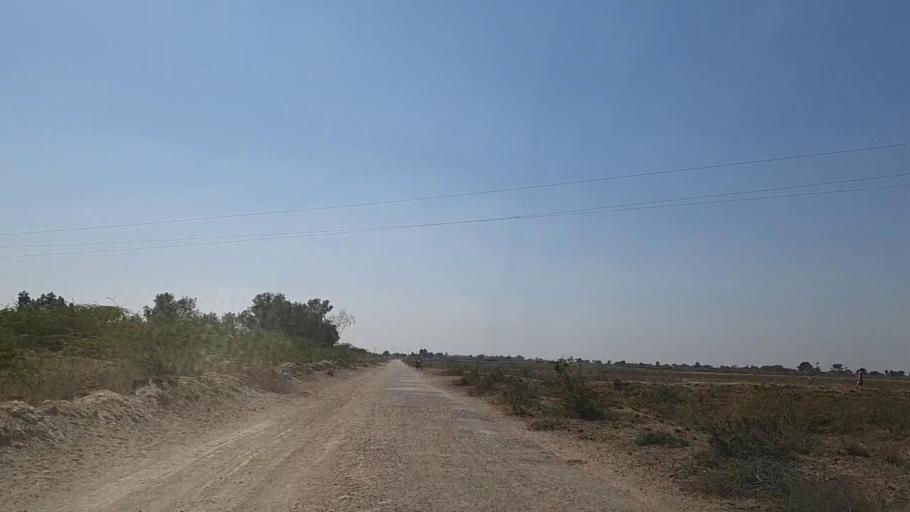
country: PK
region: Sindh
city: Pithoro
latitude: 25.4020
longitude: 69.3944
